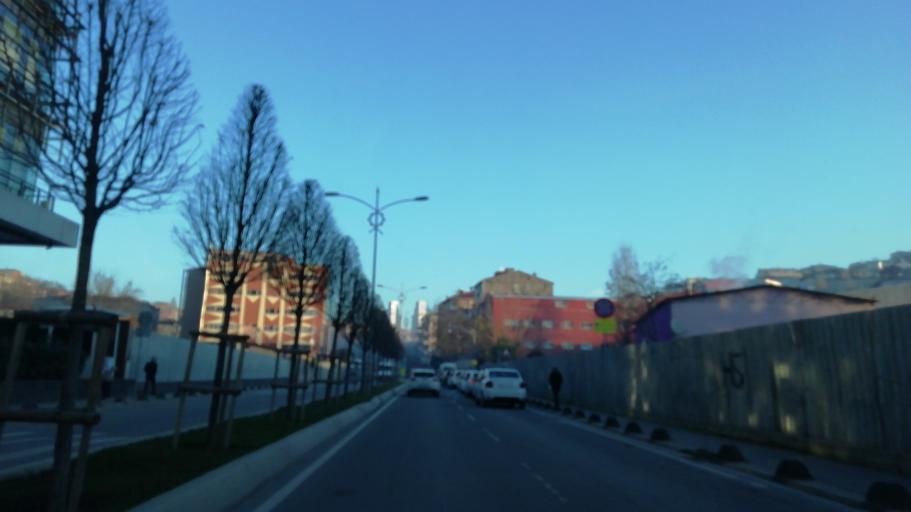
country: TR
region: Istanbul
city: Eminoenue
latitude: 41.0395
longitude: 28.9719
